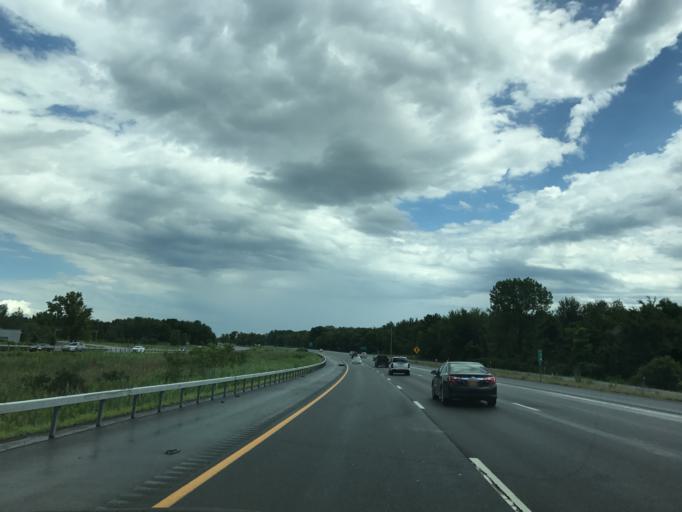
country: US
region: New York
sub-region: Albany County
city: Roessleville
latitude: 42.7291
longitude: -73.7937
